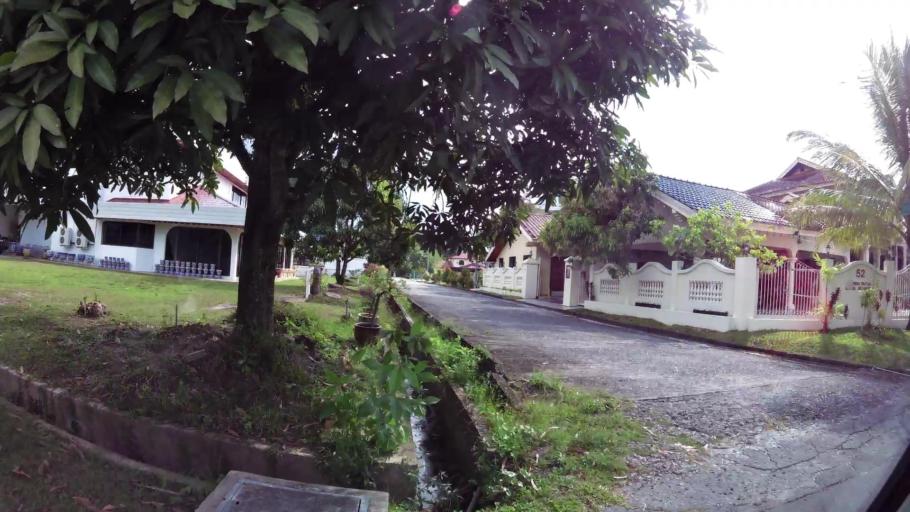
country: BN
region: Brunei and Muara
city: Bandar Seri Begawan
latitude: 4.9599
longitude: 114.9689
